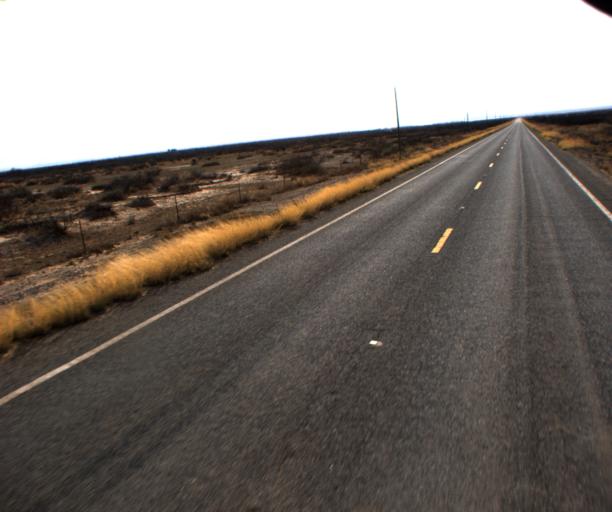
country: US
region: Arizona
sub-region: Cochise County
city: Willcox
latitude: 32.1953
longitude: -109.7268
